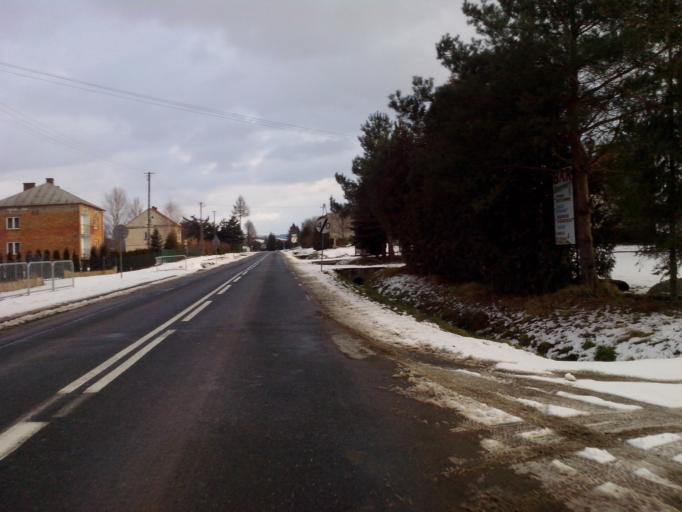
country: PL
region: Subcarpathian Voivodeship
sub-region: Powiat strzyzowski
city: Strzyzow
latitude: 49.8431
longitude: 21.8162
